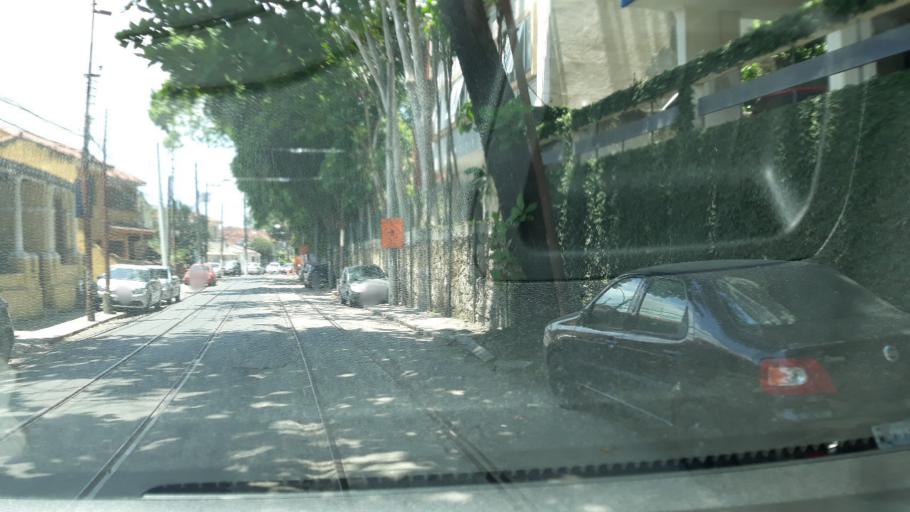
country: BR
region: Rio de Janeiro
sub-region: Rio De Janeiro
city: Rio de Janeiro
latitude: -22.9335
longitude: -43.1985
